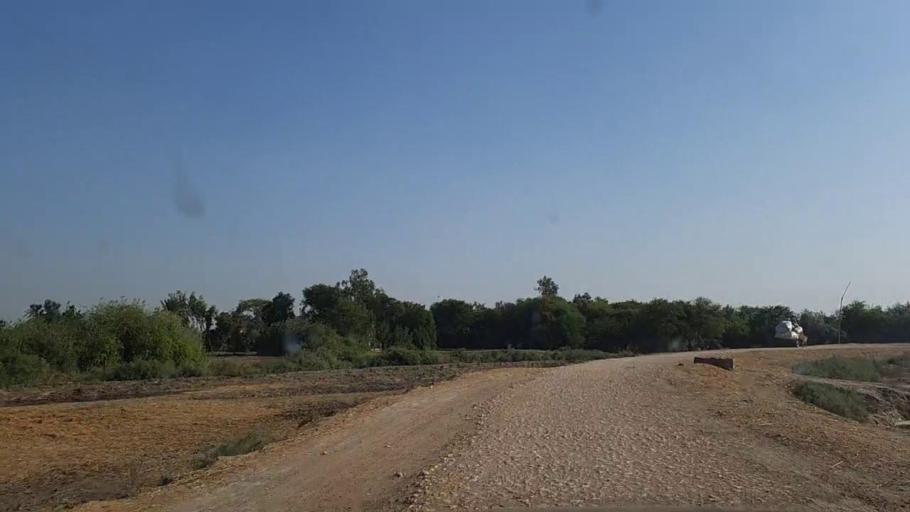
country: PK
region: Sindh
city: Daro Mehar
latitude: 24.6249
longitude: 68.0809
